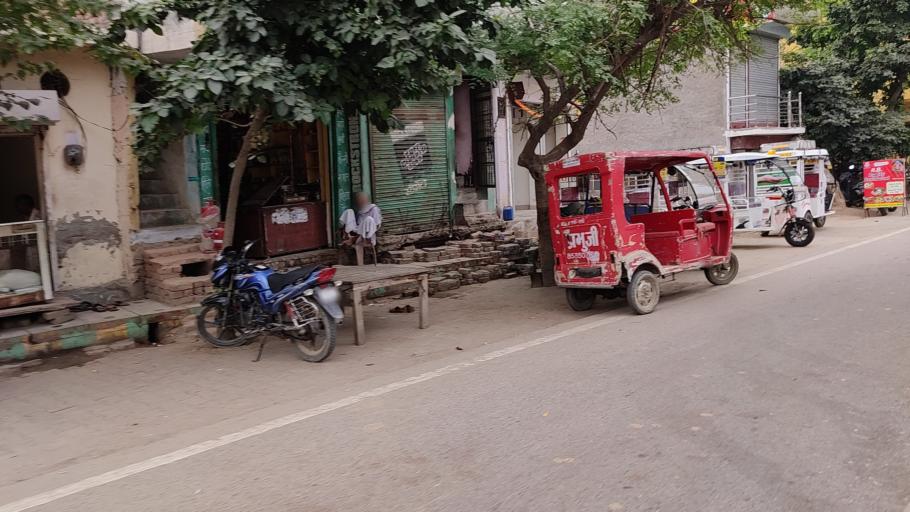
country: IN
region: Uttar Pradesh
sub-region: Mathura
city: Vrindavan
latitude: 27.5663
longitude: 77.6758
